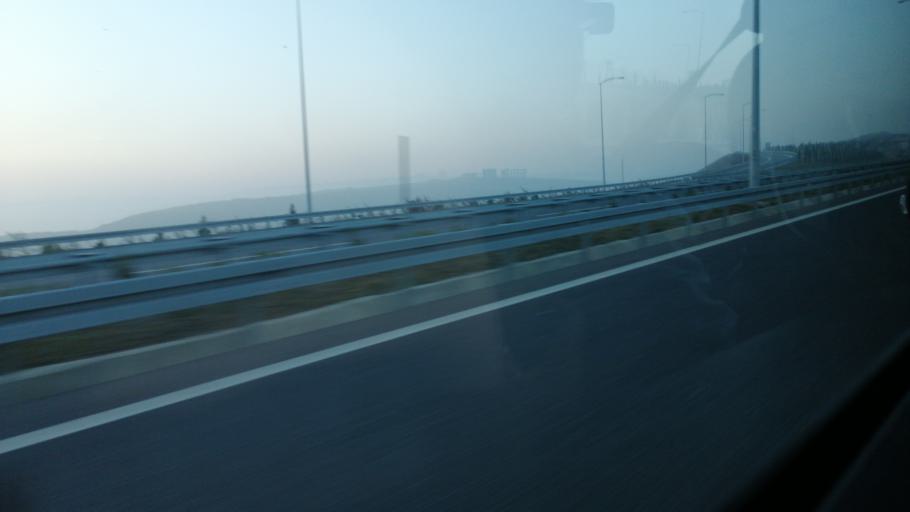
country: TR
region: Kocaeli
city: Tavsanli
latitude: 40.7732
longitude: 29.5186
